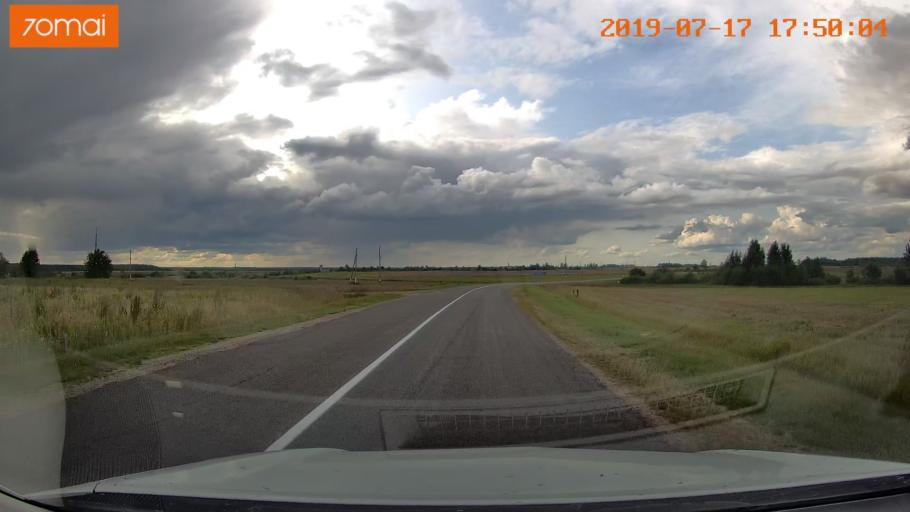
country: BY
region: Mogilev
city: Hlusha
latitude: 53.1381
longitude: 28.8036
